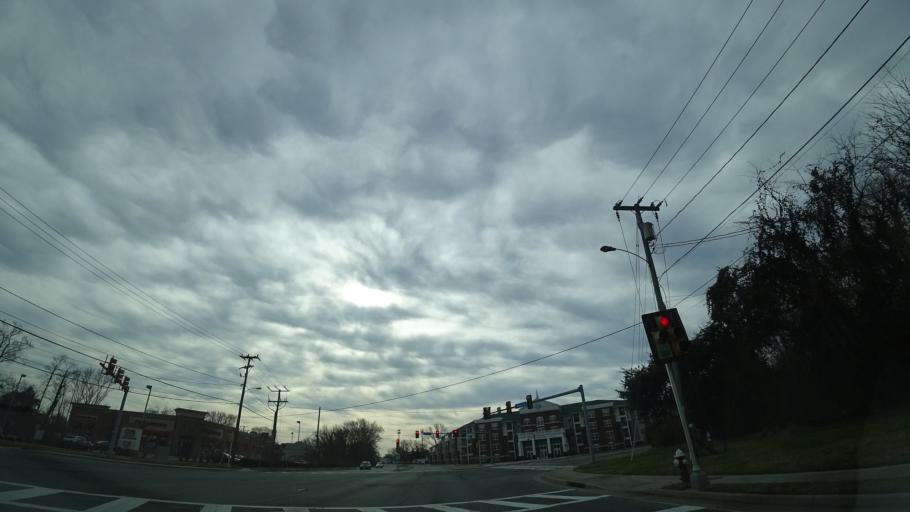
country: US
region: Virginia
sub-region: City of Hampton
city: East Hampton
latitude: 37.0273
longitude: -76.3236
